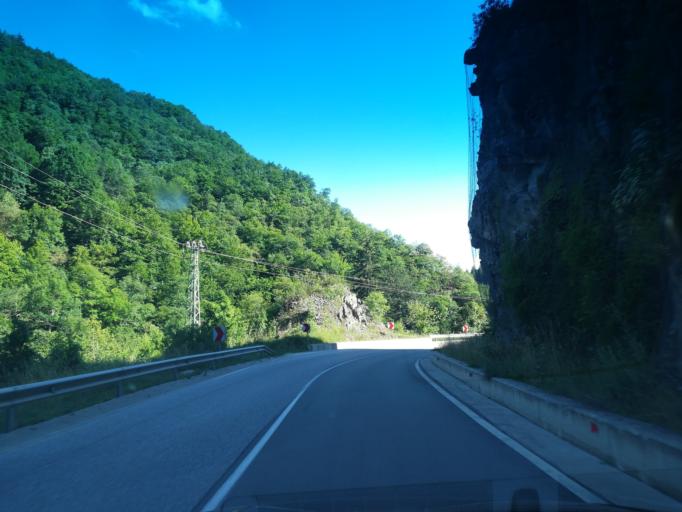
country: BG
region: Smolyan
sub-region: Obshtina Chepelare
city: Chepelare
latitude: 41.7835
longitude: 24.7080
